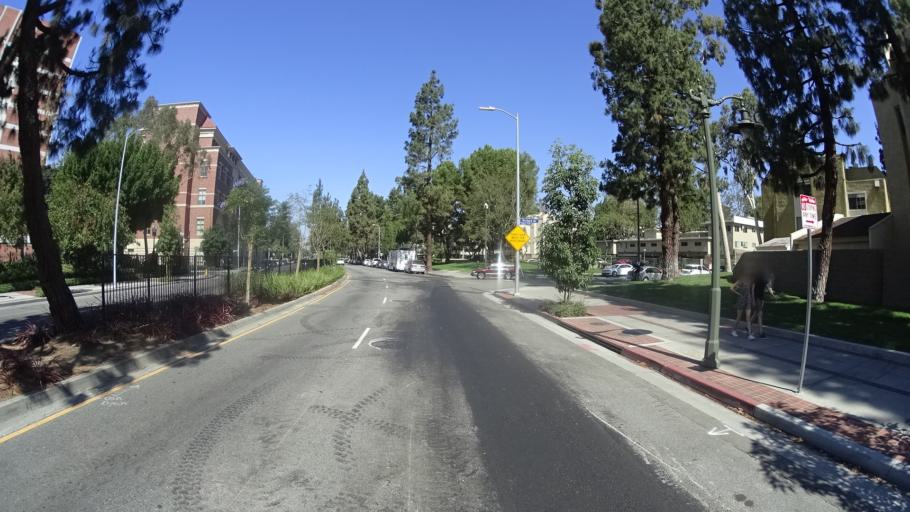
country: US
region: California
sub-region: Los Angeles County
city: Los Angeles
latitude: 34.0255
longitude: -118.2879
